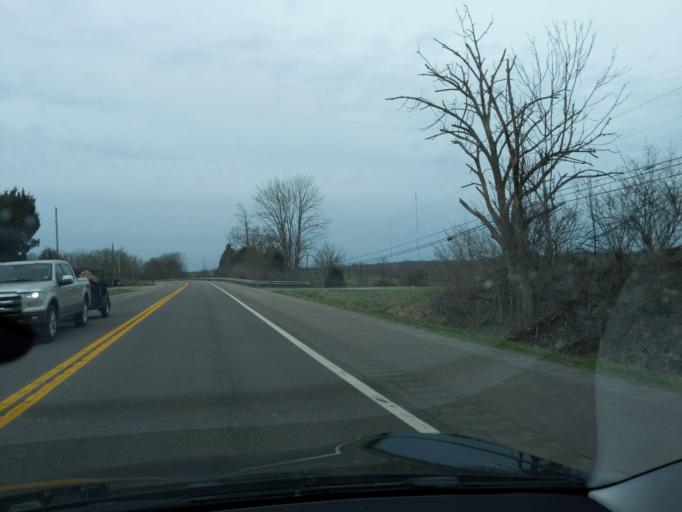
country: US
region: Kentucky
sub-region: Madison County
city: Richmond
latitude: 37.8826
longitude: -84.2924
